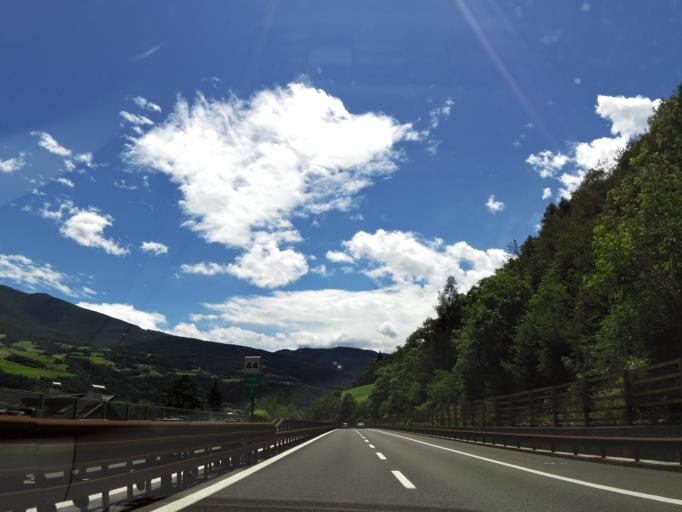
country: IT
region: Trentino-Alto Adige
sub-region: Bolzano
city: Bressanone
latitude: 46.7126
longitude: 11.6475
